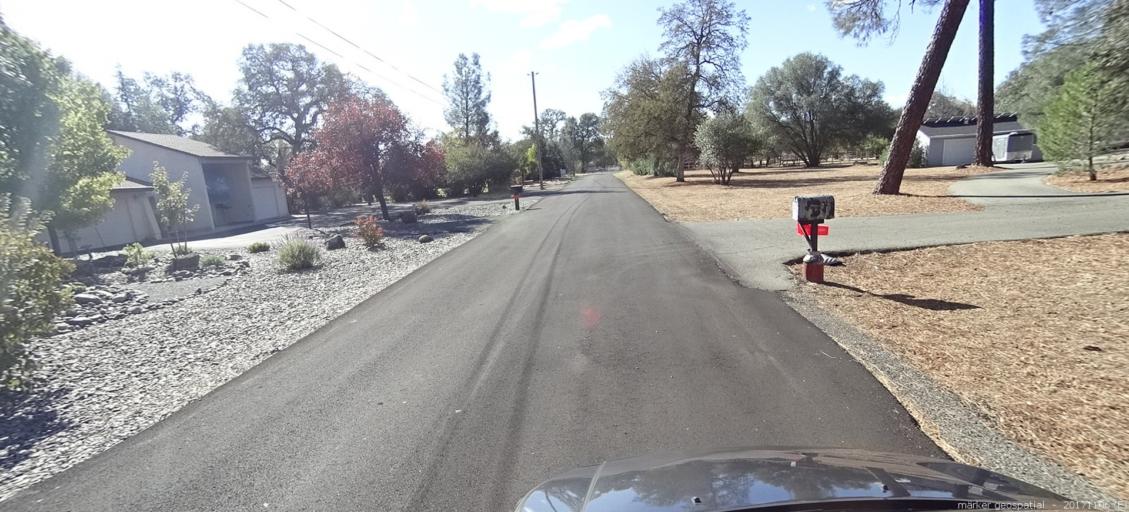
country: US
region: California
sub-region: Shasta County
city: Palo Cedro
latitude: 40.5894
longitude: -122.2220
